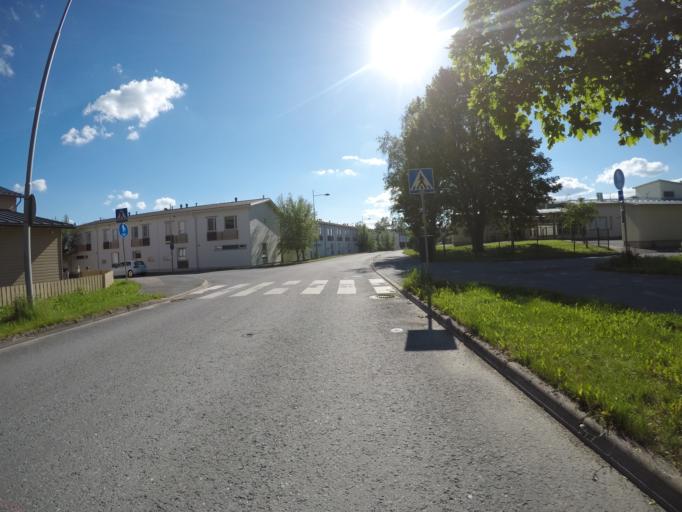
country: FI
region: Haeme
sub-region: Haemeenlinna
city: Haemeenlinna
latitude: 60.9803
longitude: 24.4784
